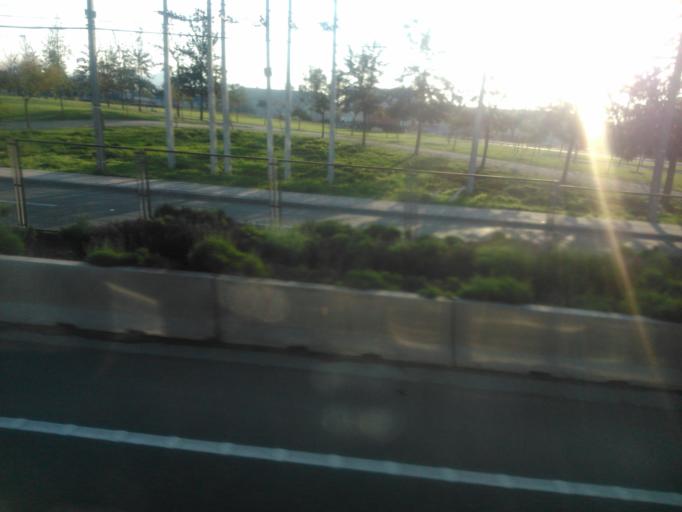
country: CL
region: Santiago Metropolitan
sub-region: Provincia de Maipo
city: San Bernardo
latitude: -33.6258
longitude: -70.7144
